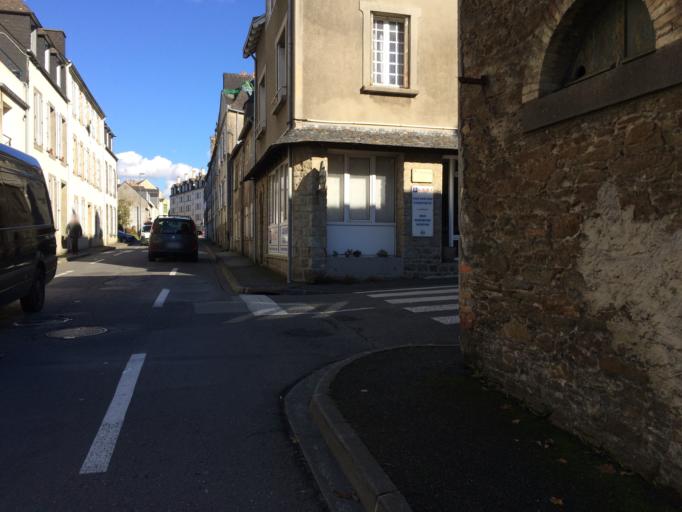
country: FR
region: Brittany
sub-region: Departement du Finistere
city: Landerneau
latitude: 48.4489
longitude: -4.2474
